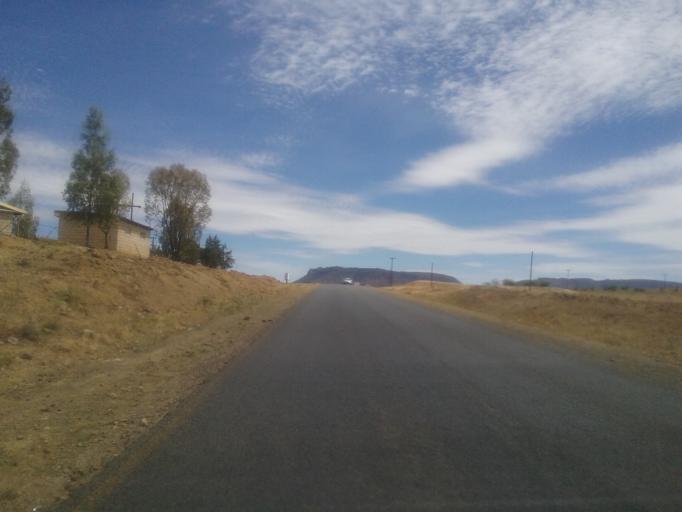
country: LS
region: Mafeteng
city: Mafeteng
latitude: -29.9820
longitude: 27.3239
